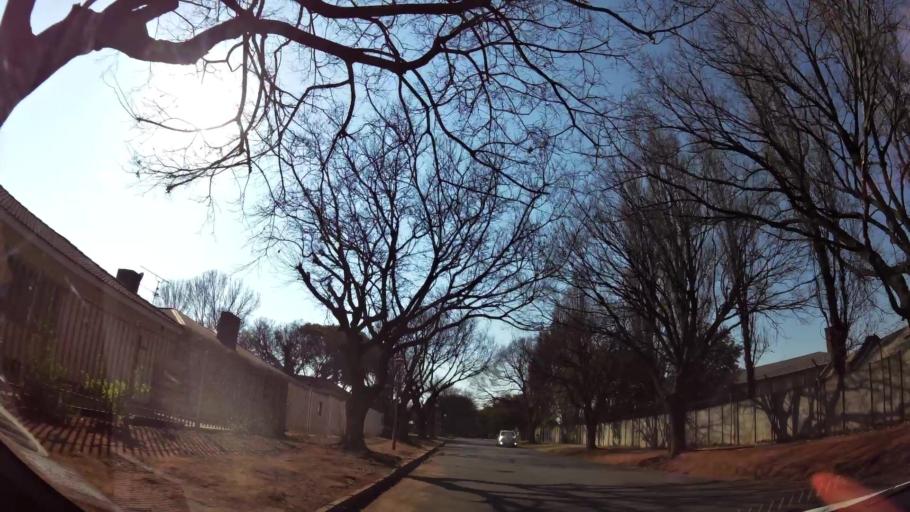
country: ZA
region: Gauteng
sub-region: Ekurhuleni Metropolitan Municipality
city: Boksburg
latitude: -26.2288
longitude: 28.2699
